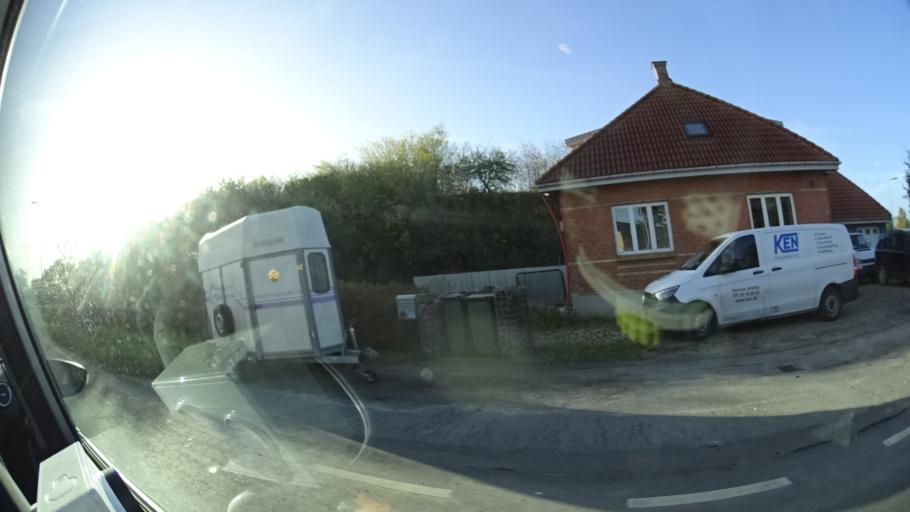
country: DK
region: South Denmark
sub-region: Odense Kommune
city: Hojby
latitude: 55.3388
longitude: 10.4365
